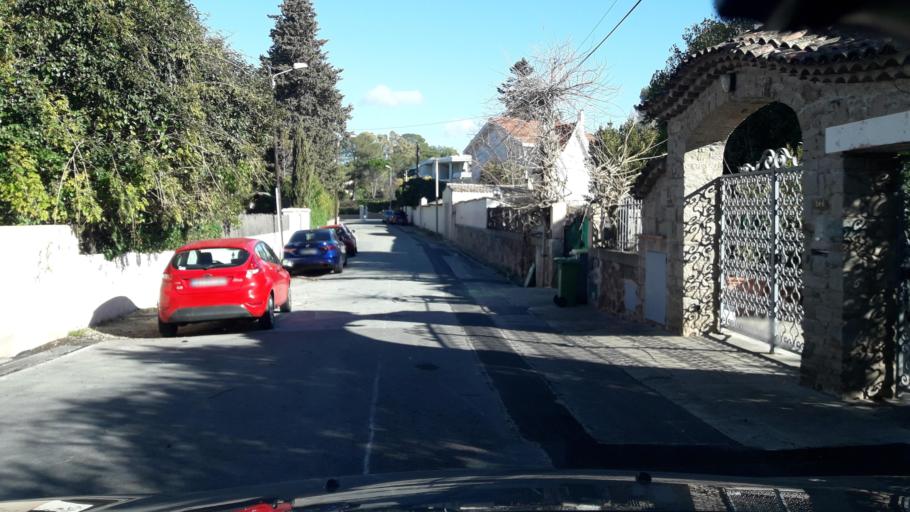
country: FR
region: Provence-Alpes-Cote d'Azur
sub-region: Departement du Var
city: Saint-Raphael
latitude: 43.4427
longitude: 6.7759
